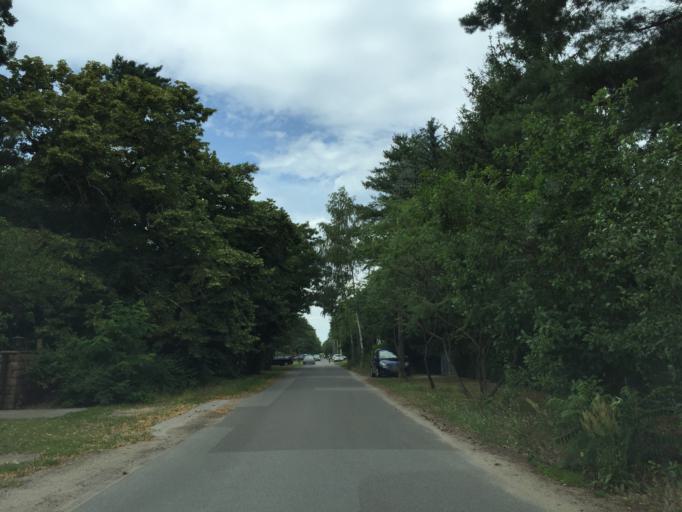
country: DE
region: Berlin
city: Mahlsdorf
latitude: 52.4881
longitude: 13.6214
